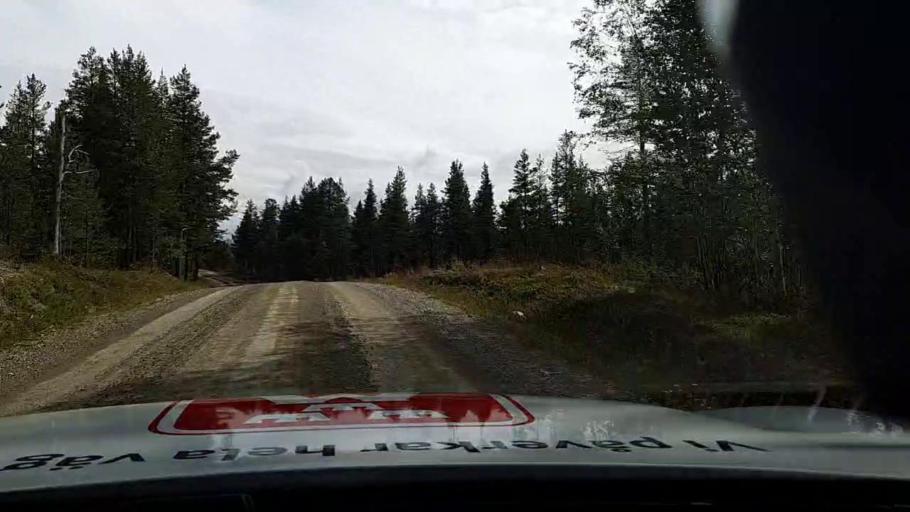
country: SE
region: Jaemtland
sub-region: Are Kommun
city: Jarpen
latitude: 62.5145
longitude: 13.4883
